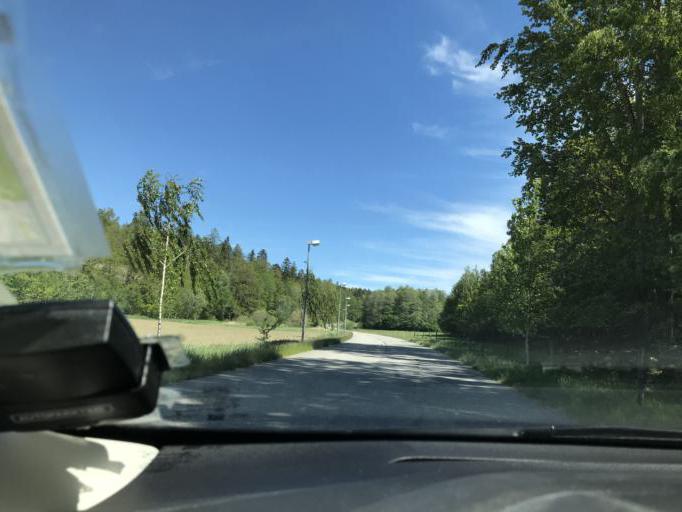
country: SE
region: Stockholm
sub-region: Botkyrka Kommun
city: Tumba
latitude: 59.2186
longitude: 17.8357
